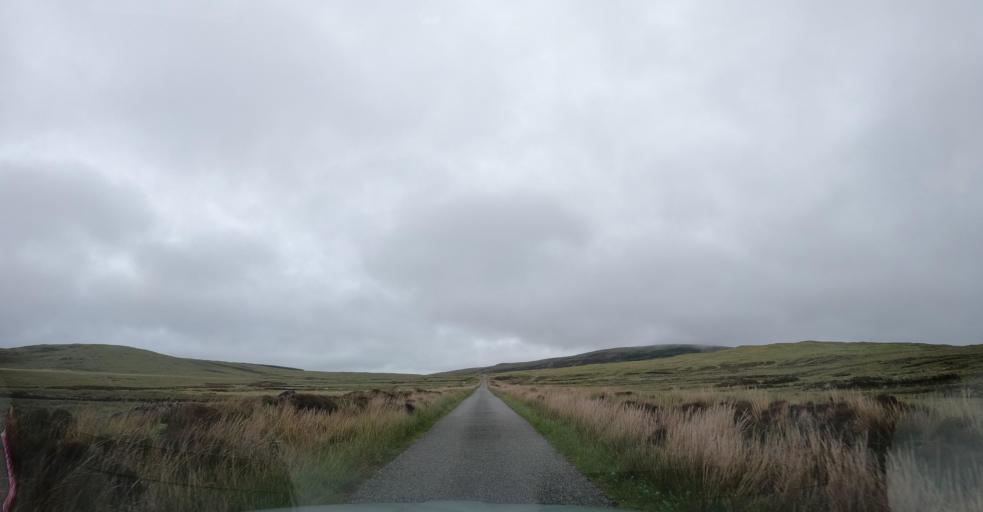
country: GB
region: Scotland
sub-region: Eilean Siar
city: Isle of North Uist
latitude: 57.6002
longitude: -7.3845
